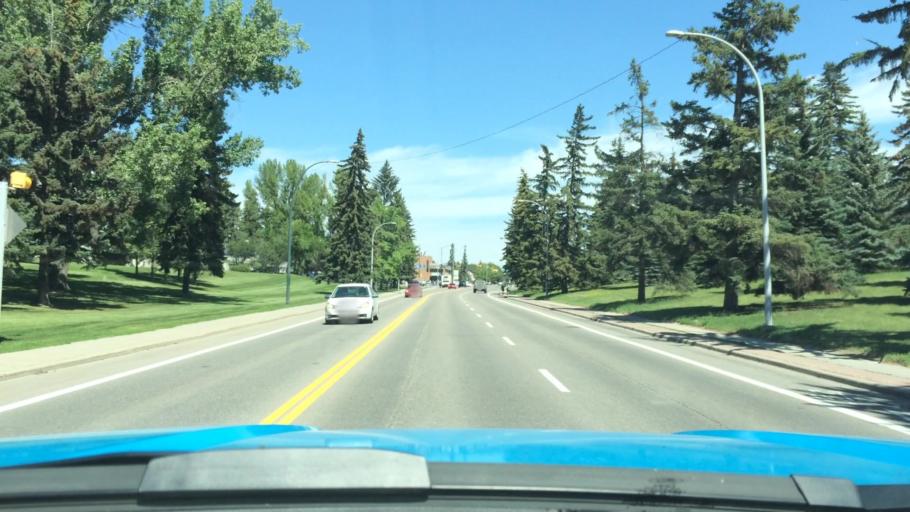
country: CA
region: Alberta
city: Calgary
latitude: 51.0644
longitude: -114.0846
